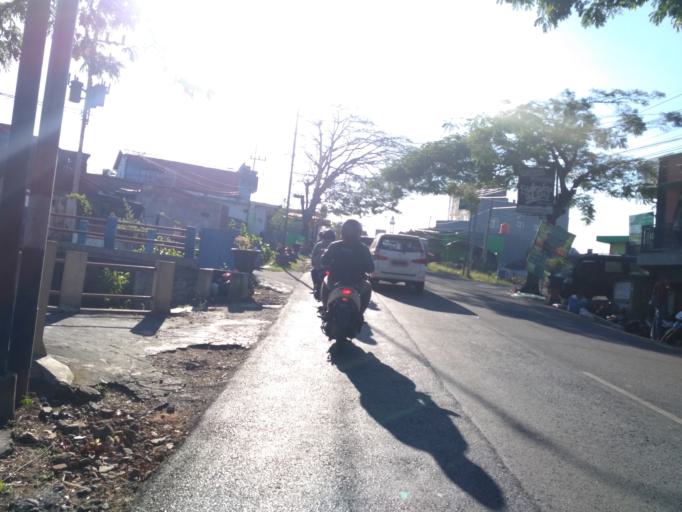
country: ID
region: East Java
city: Batu
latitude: -7.8927
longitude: 112.5498
